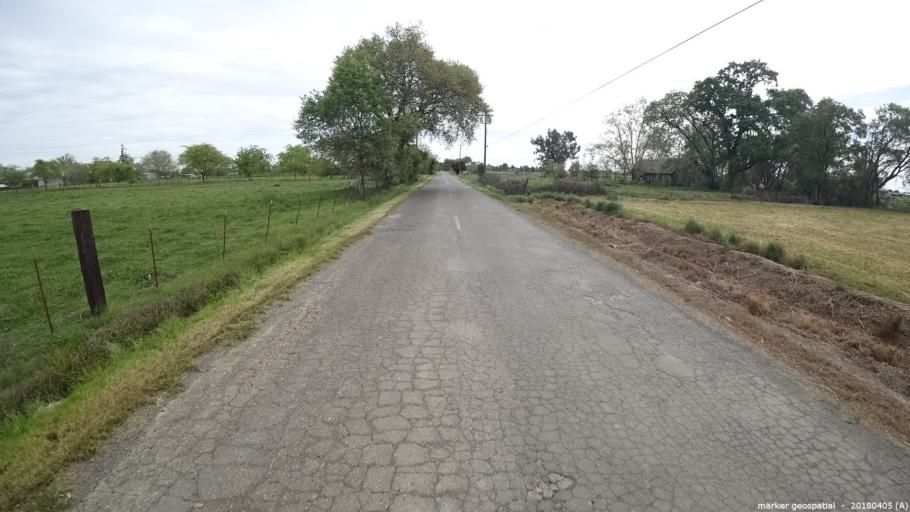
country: US
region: California
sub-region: Sacramento County
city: Galt
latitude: 38.2545
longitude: -121.3478
